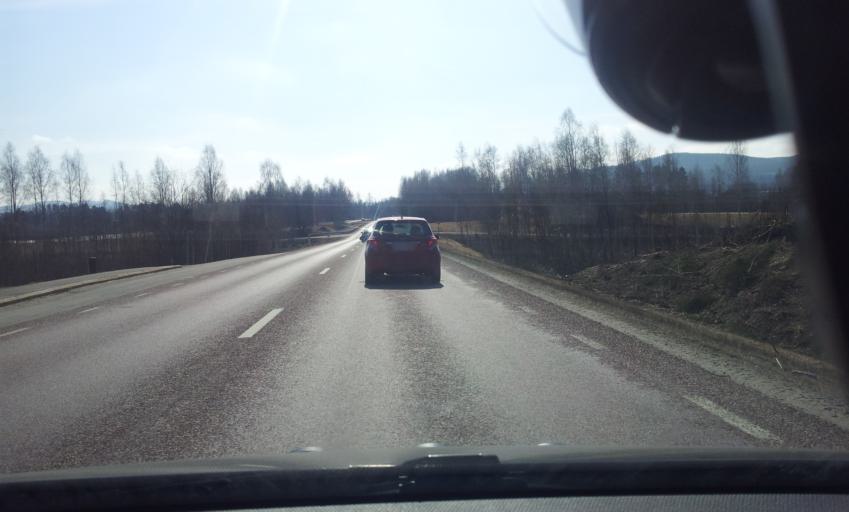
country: SE
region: Gaevleborg
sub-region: Ljusdals Kommun
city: Jaervsoe
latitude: 61.7662
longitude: 16.1577
